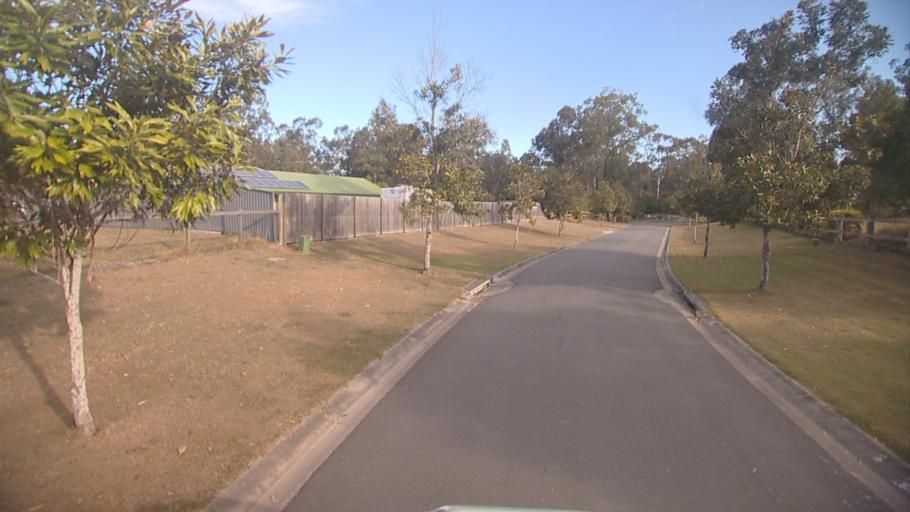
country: AU
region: Queensland
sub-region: Logan
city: North Maclean
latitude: -27.8032
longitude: 152.9687
